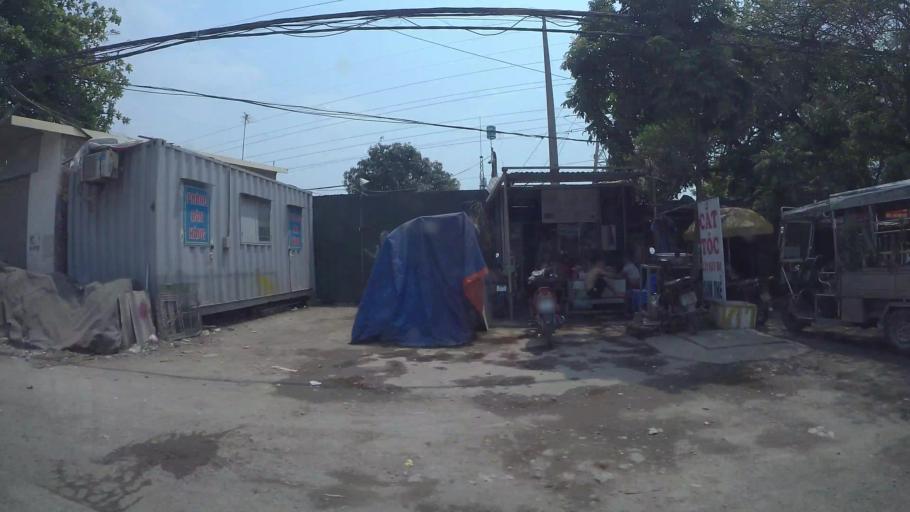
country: VN
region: Ha Noi
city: Van Dien
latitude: 20.9435
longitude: 105.8403
